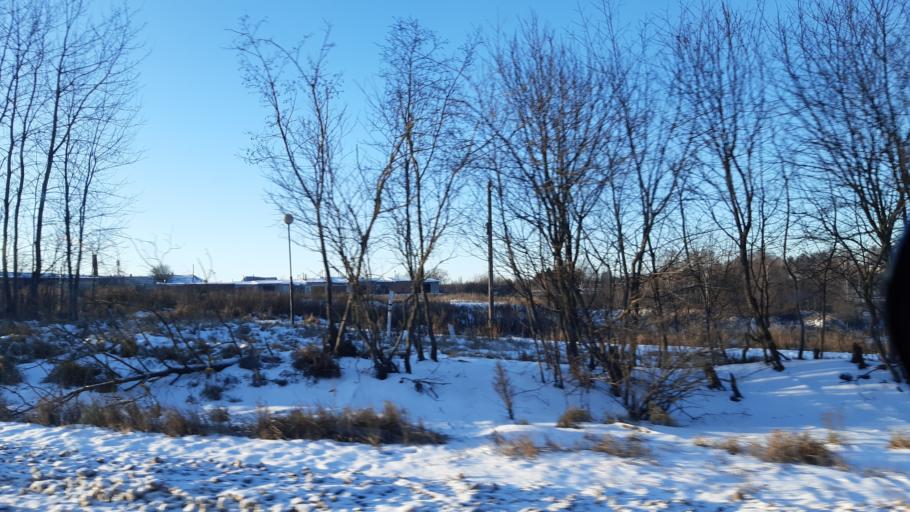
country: RU
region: Moskovskaya
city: Skoropuskovskiy
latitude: 56.3431
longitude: 38.1682
